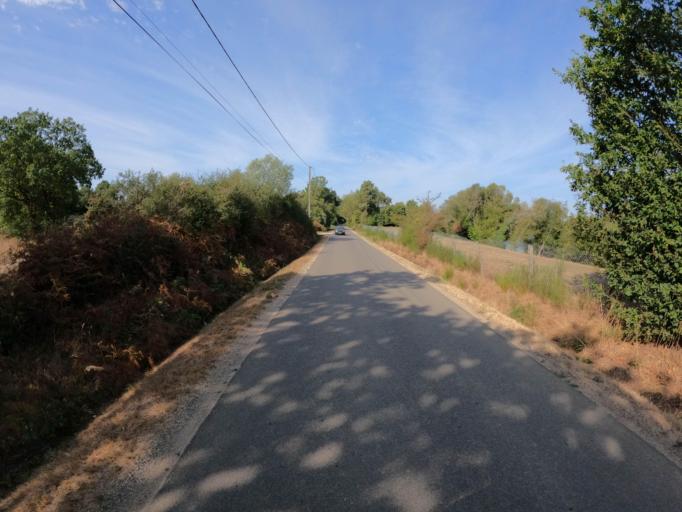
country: FR
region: Pays de la Loire
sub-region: Departement de la Vendee
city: Commequiers
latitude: 46.8111
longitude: -1.8347
